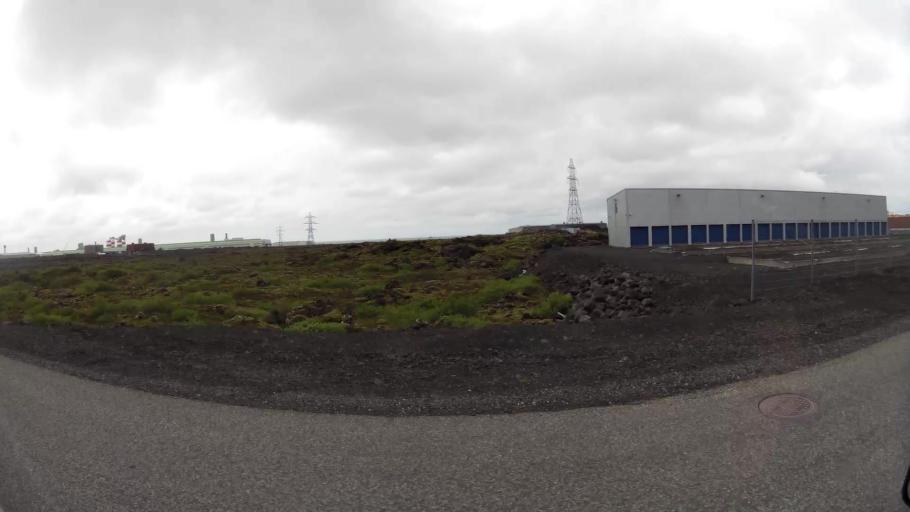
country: IS
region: Capital Region
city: Alftanes
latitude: 64.0415
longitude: -22.0044
